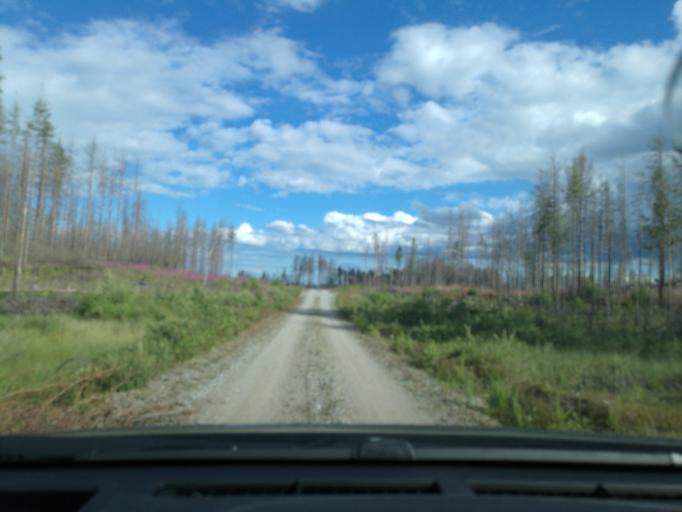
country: SE
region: Vaestmanland
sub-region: Surahammars Kommun
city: Ramnas
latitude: 59.8528
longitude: 16.2532
